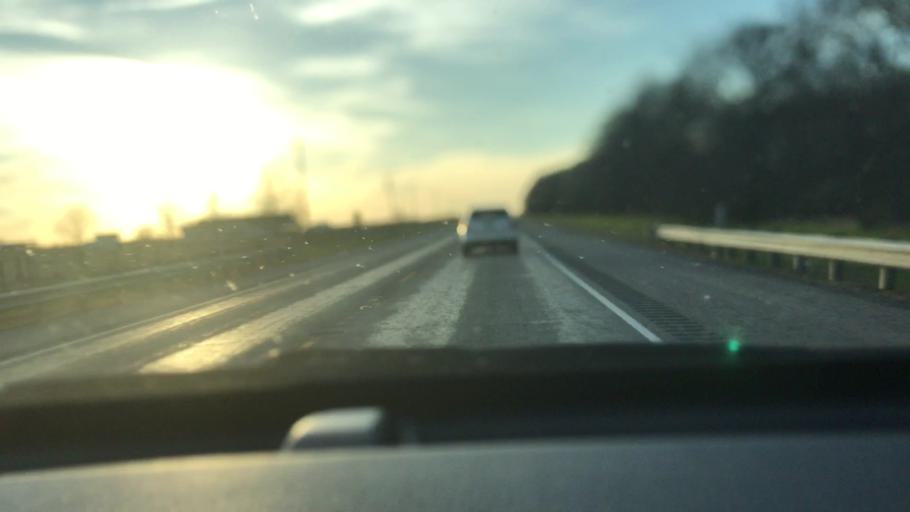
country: US
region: Texas
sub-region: Red River County
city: Clarksville
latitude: 33.6073
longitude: -95.0078
